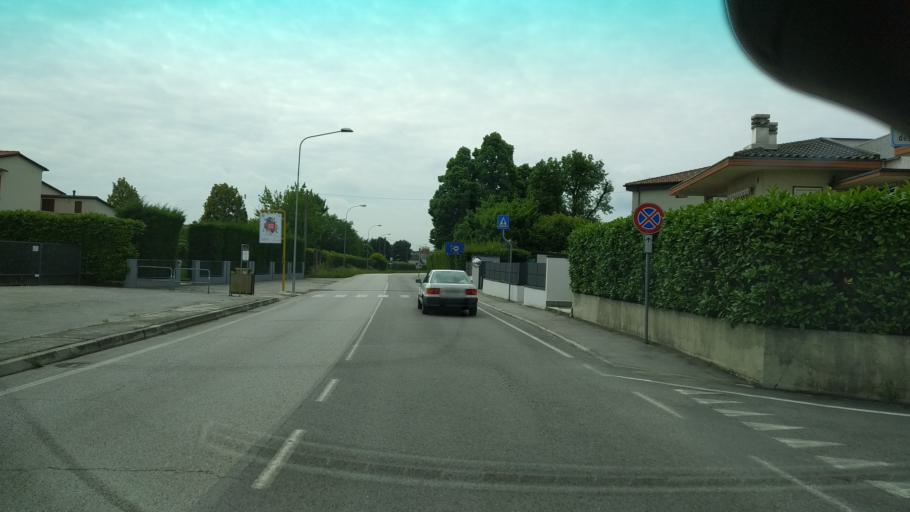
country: IT
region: Veneto
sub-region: Provincia di Vicenza
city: Crispi Cavour
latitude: 45.5931
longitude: 11.5264
